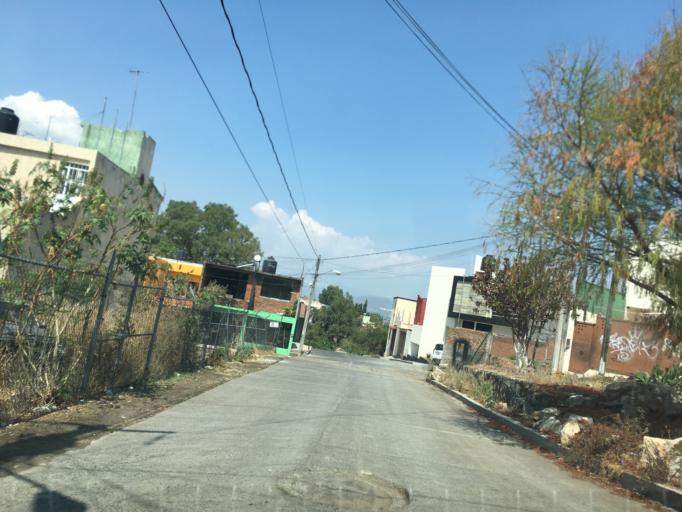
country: MX
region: Michoacan
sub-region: Morelia
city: Montana Monarca (Punta Altozano)
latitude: 19.6697
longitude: -101.1953
